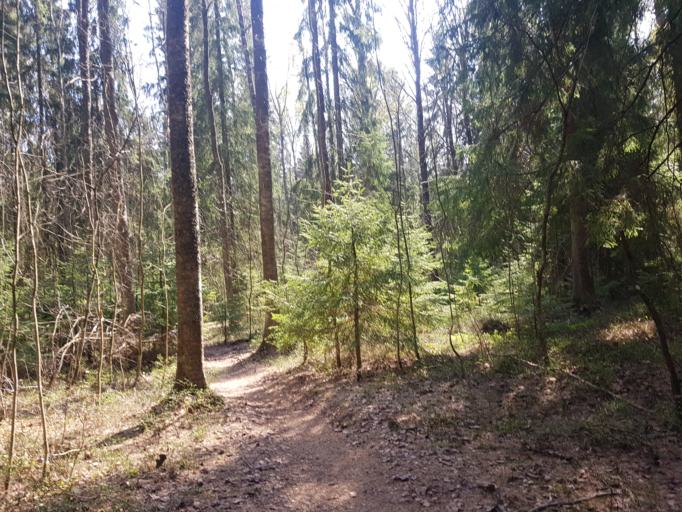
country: FI
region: Uusimaa
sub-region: Helsinki
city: Helsinki
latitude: 60.2666
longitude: 24.9187
